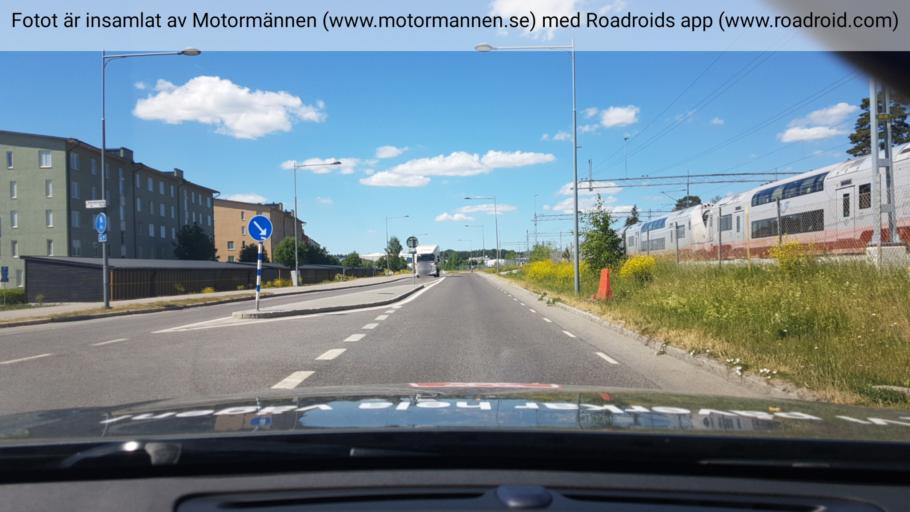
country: SE
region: Stockholm
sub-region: Stockholms Kommun
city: Kista
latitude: 59.3845
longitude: 17.8958
